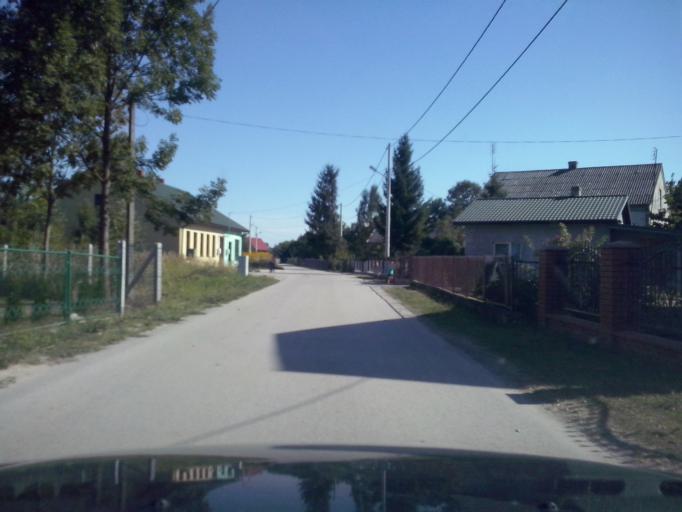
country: PL
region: Swietokrzyskie
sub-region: Powiat kielecki
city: Chmielnik
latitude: 50.6173
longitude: 20.7034
